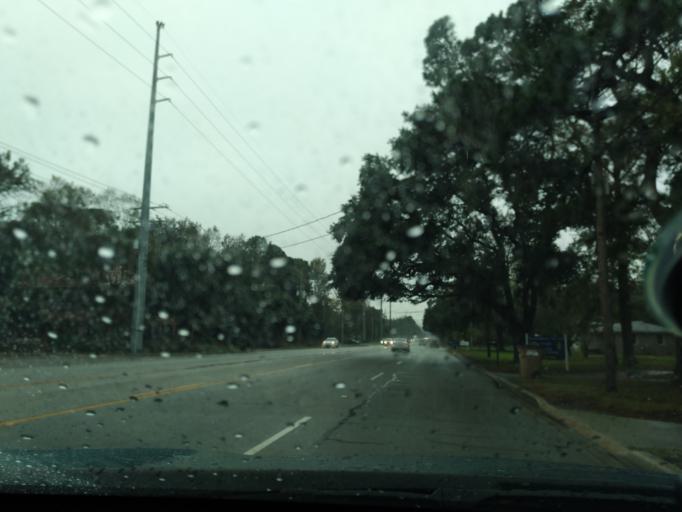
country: US
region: South Carolina
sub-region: Charleston County
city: Charleston
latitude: 32.7189
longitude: -79.9661
